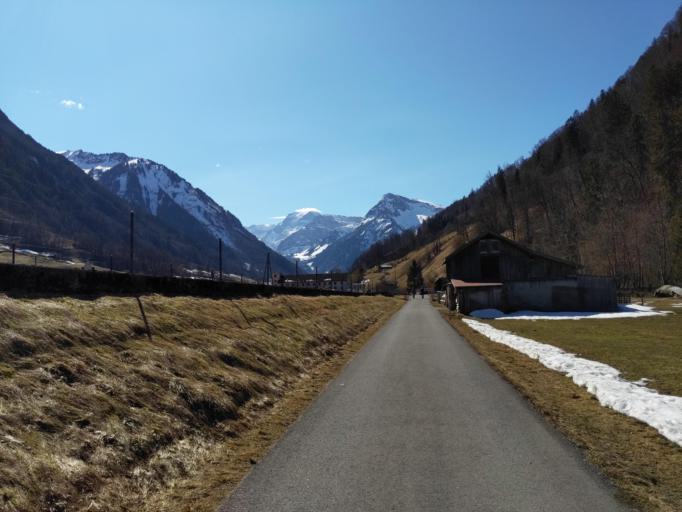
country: CH
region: Glarus
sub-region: Glarus
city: Luchsingen
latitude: 46.9487
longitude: 9.0254
